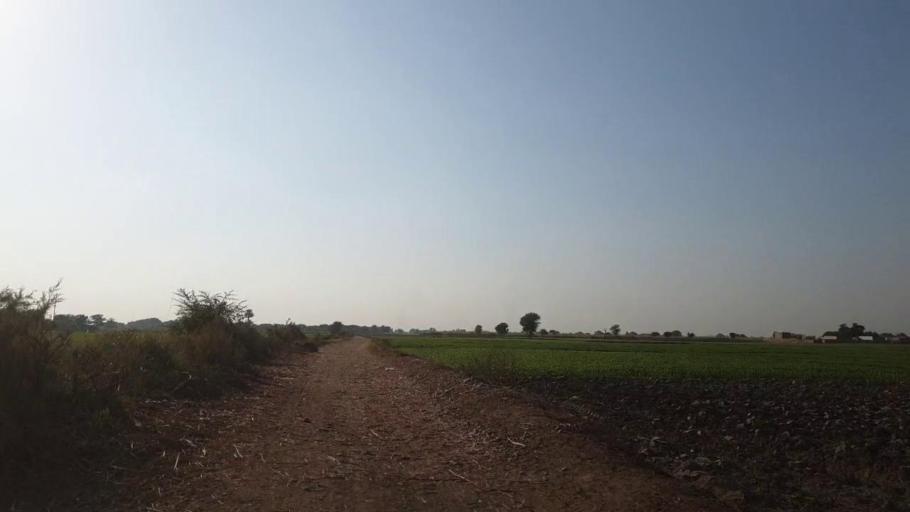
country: PK
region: Sindh
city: Tando Allahyar
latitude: 25.5762
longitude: 68.6551
